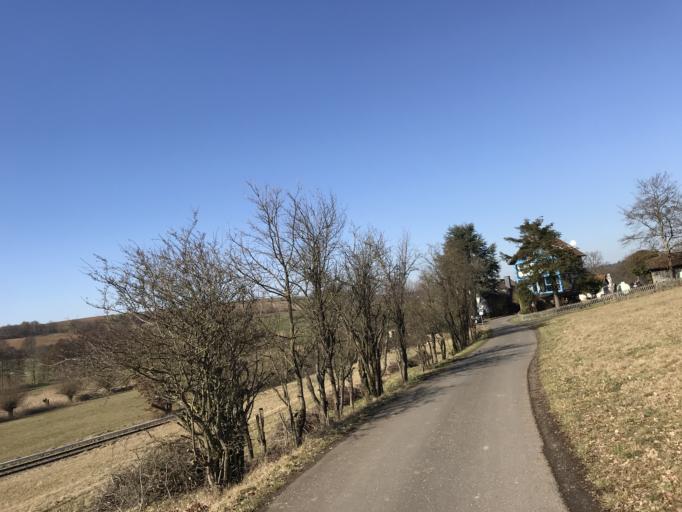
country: DE
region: Hesse
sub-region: Regierungsbezirk Darmstadt
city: Nidda
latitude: 50.3897
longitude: 8.9789
